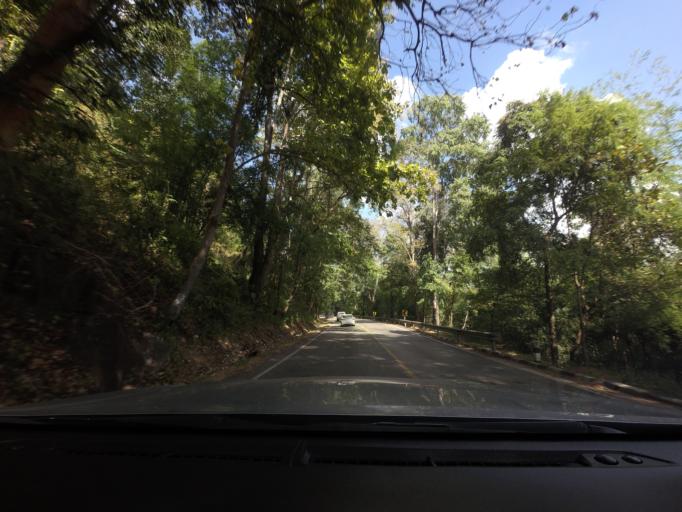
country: TH
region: Chiang Mai
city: Chai Prakan
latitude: 19.6024
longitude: 99.1187
